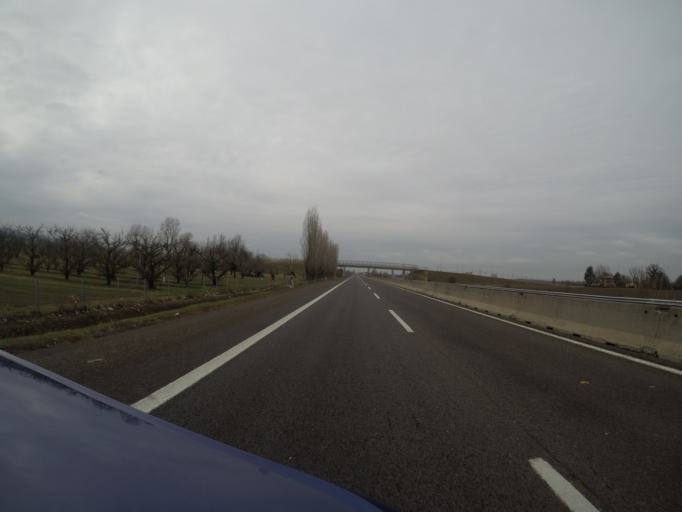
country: IT
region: Emilia-Romagna
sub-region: Provincia di Bologna
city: Zola Predosa
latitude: 44.5015
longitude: 11.2170
